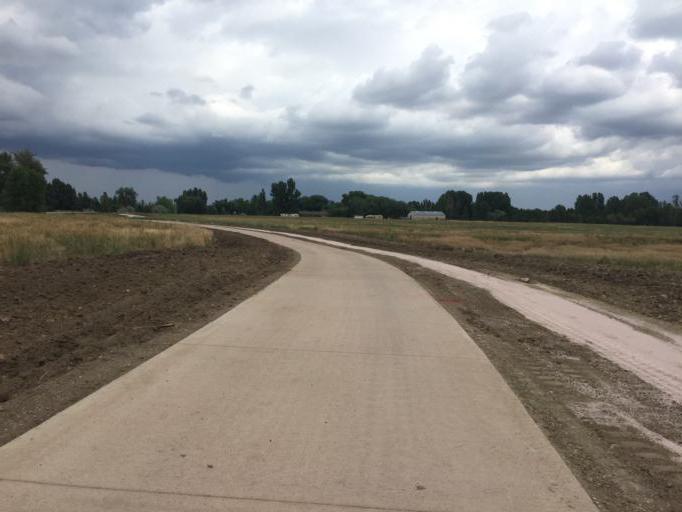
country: US
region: Colorado
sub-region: Larimer County
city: Fort Collins
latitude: 40.5011
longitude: -105.0956
